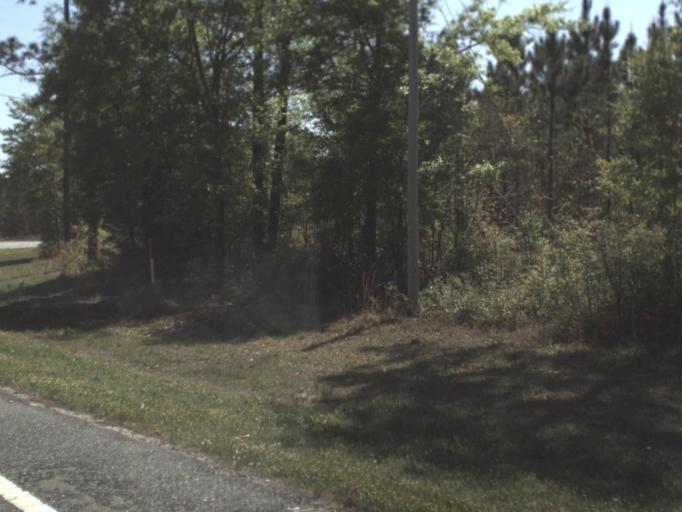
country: US
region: Alabama
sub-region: Escambia County
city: East Brewton
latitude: 30.9067
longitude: -87.0351
